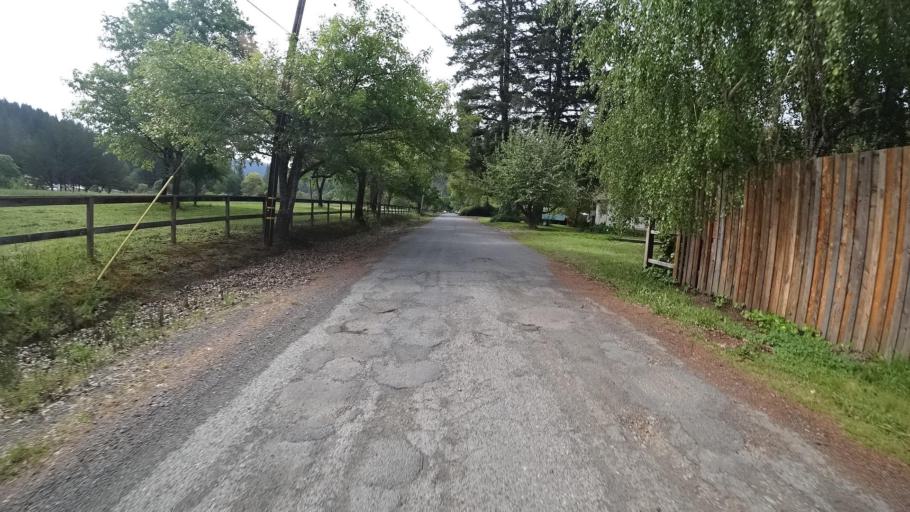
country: US
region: California
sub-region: Humboldt County
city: Redway
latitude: 40.2111
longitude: -123.7899
